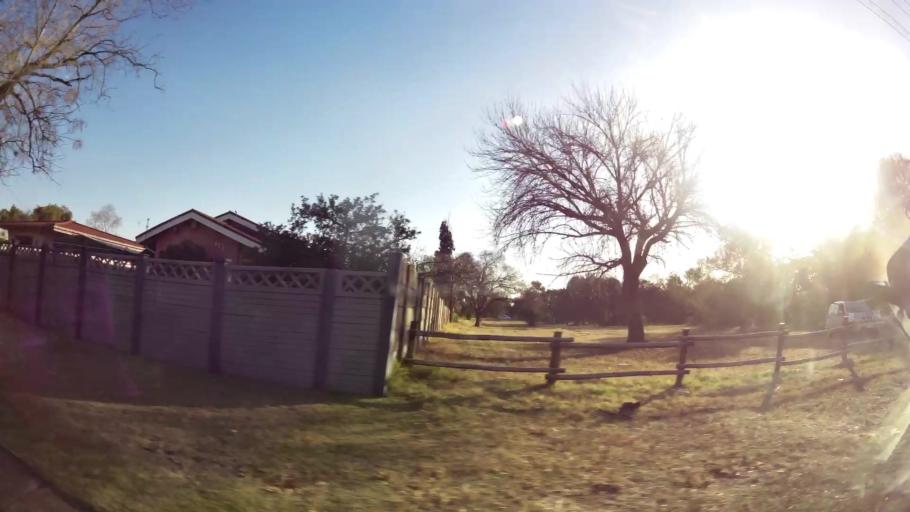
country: ZA
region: Gauteng
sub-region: City of Tshwane Metropolitan Municipality
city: Pretoria
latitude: -25.7039
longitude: 28.2048
